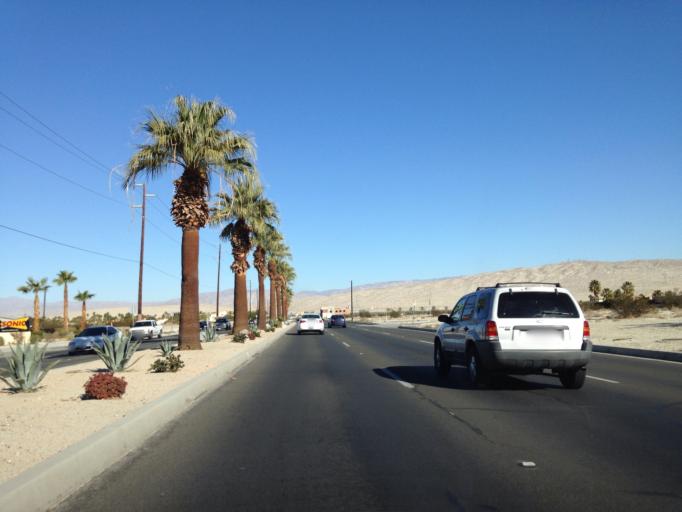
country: US
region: California
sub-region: Riverside County
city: Cathedral City
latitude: 33.8245
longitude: -116.4581
